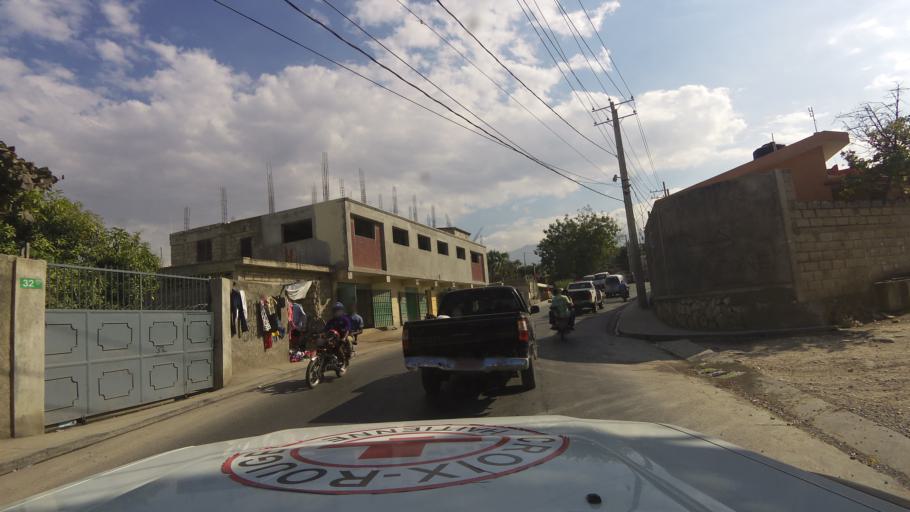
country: HT
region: Ouest
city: Delmas 73
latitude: 18.5425
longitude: -72.2883
